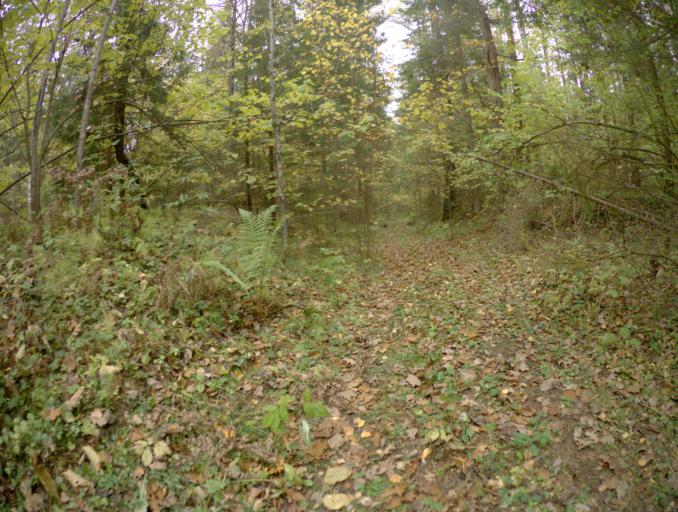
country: RU
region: Vladimir
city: Stepantsevo
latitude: 56.3093
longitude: 41.7215
